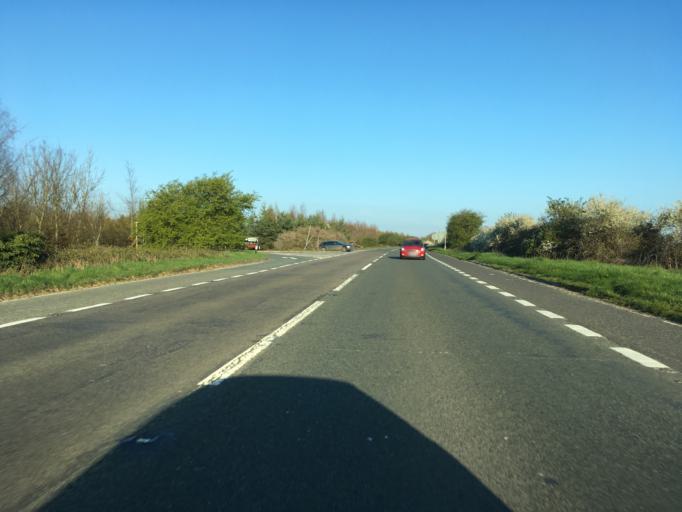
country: GB
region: England
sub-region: Oxfordshire
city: Burford
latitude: 51.8076
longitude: -1.6614
